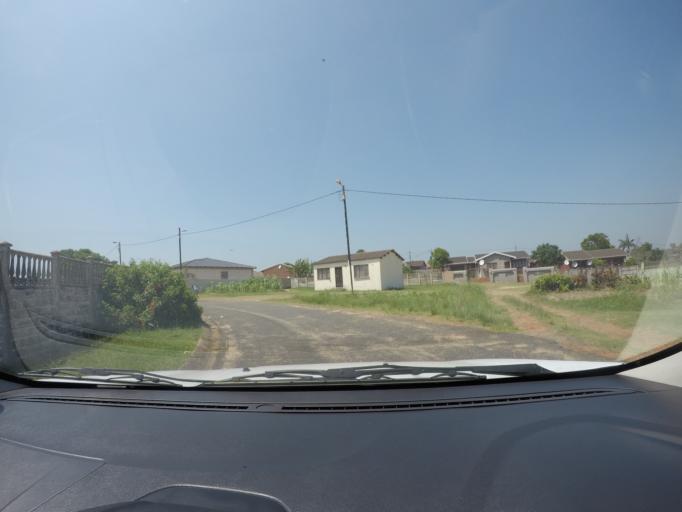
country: ZA
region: KwaZulu-Natal
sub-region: uThungulu District Municipality
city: eSikhawini
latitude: -28.8681
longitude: 31.9237
